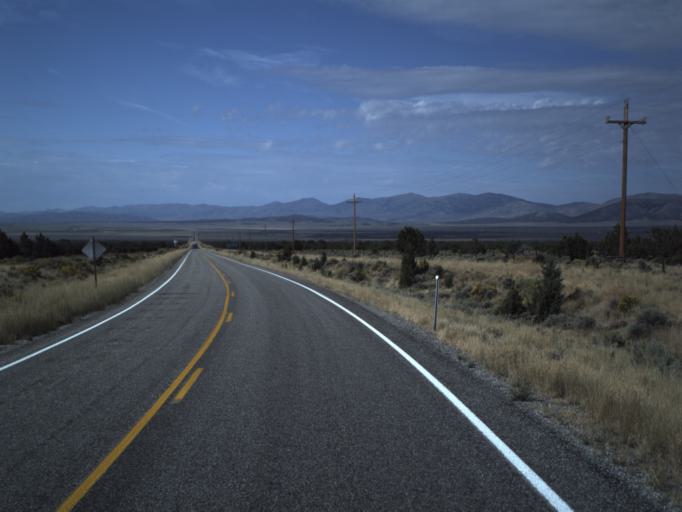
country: US
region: Idaho
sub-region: Cassia County
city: Burley
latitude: 41.8198
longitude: -113.4293
